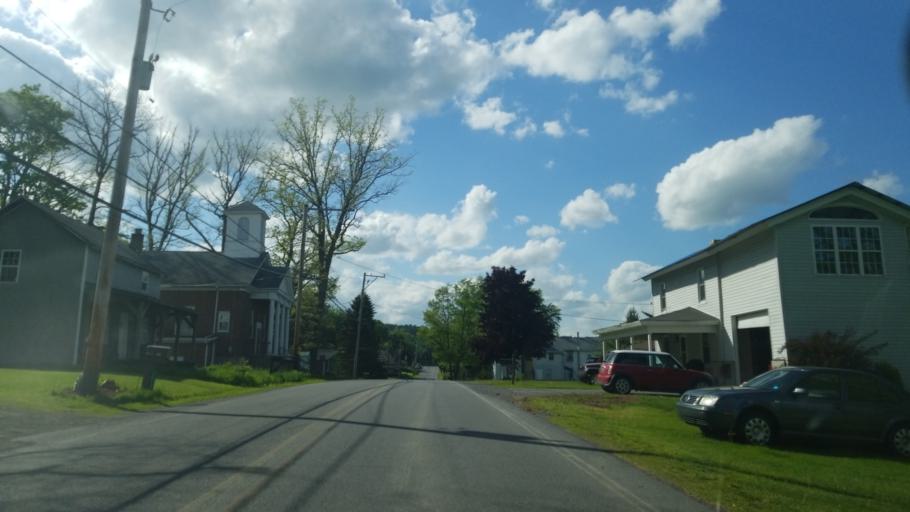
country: US
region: Pennsylvania
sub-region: Clearfield County
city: Troy
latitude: 40.9242
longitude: -78.2758
